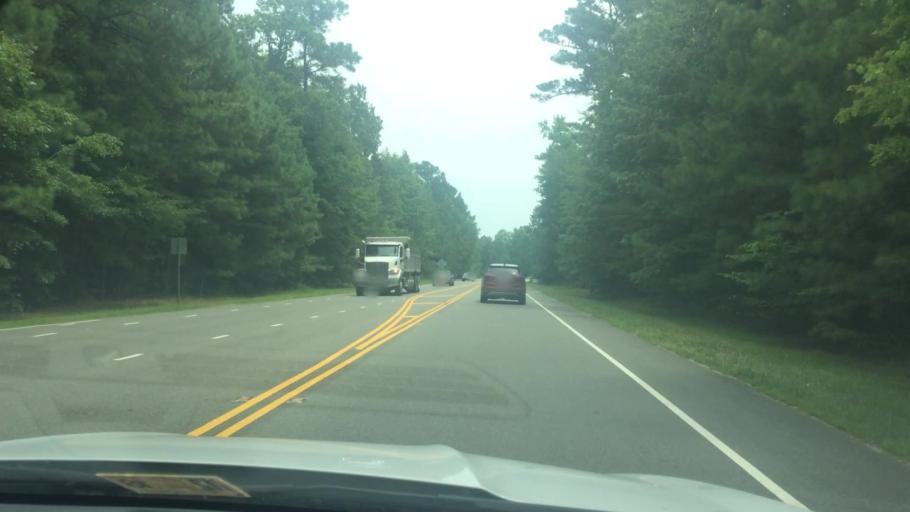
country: US
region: Virginia
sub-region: James City County
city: Williamsburg
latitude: 37.2636
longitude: -76.8040
